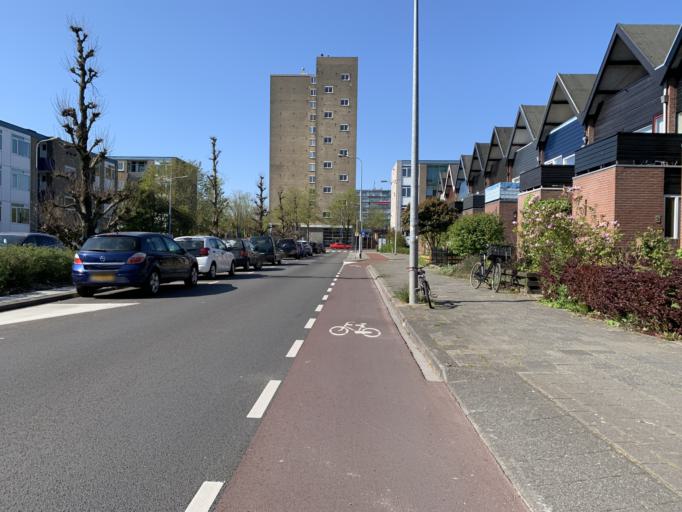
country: NL
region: Groningen
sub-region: Gemeente Groningen
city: Korrewegwijk
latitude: 53.2320
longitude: 6.5536
